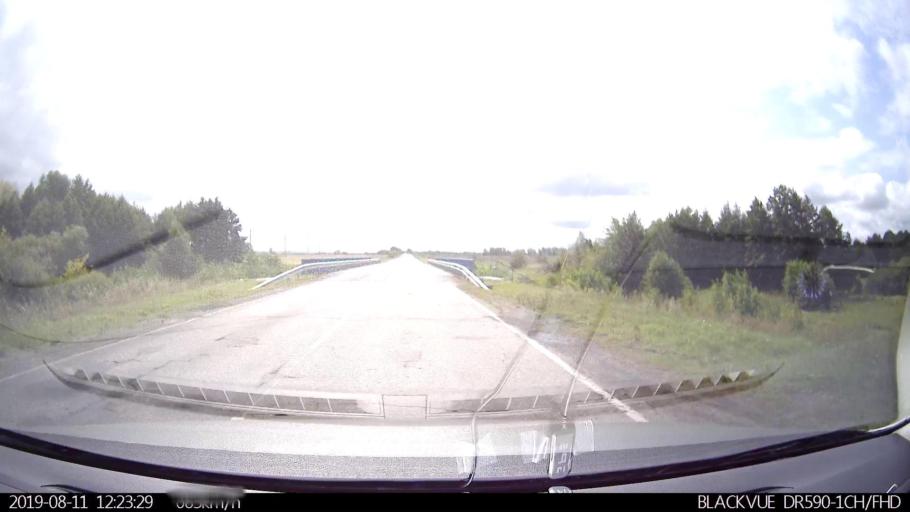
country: RU
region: Ulyanovsk
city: Ignatovka
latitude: 53.8945
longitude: 47.9504
